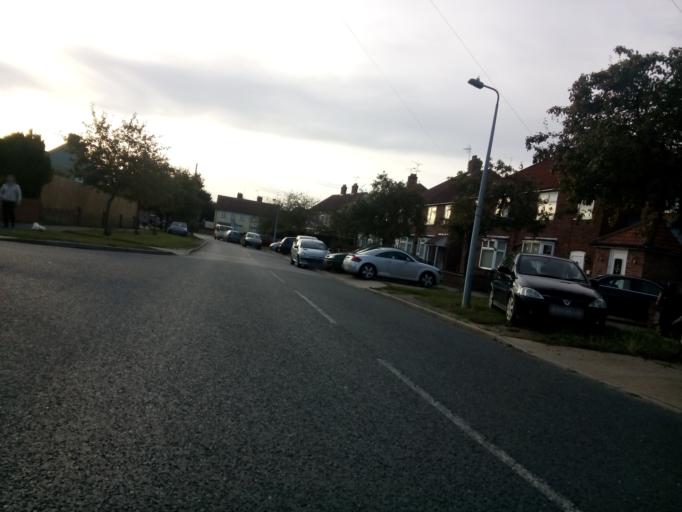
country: GB
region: England
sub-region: Suffolk
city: Bramford
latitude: 52.0796
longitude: 1.1294
